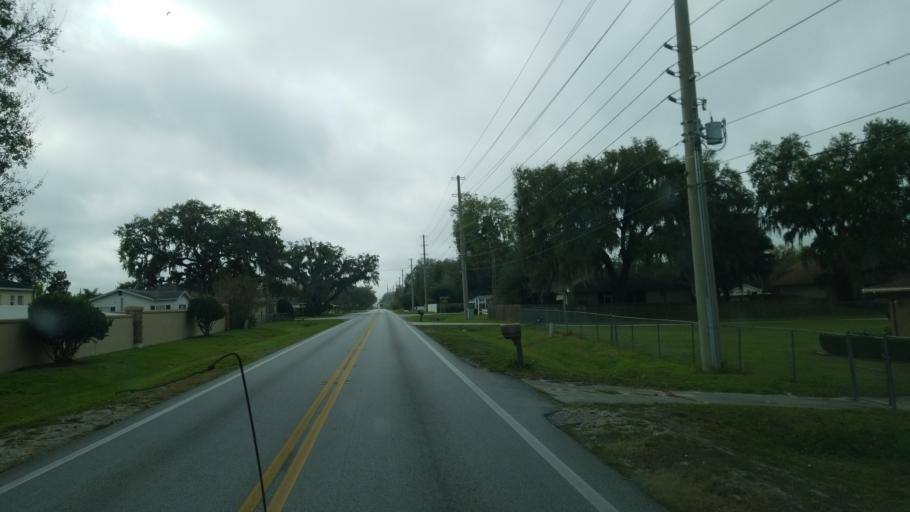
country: US
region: Florida
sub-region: Polk County
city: Kathleen
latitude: 28.0885
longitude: -82.0068
